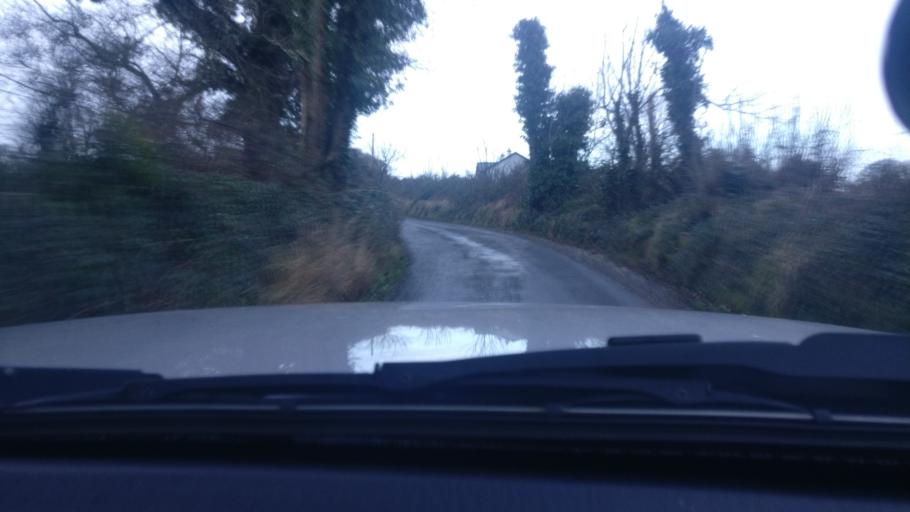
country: IE
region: Connaught
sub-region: County Galway
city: Loughrea
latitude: 53.1779
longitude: -8.5086
